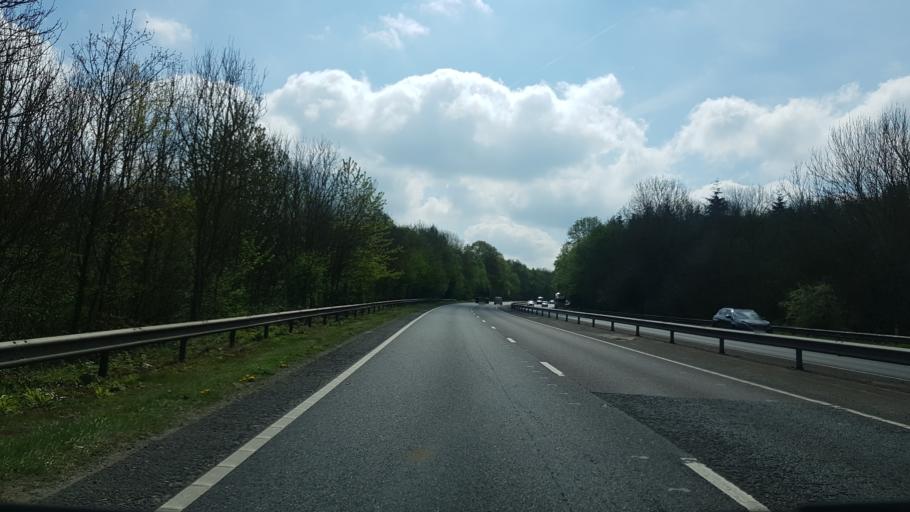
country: GB
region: England
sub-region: Kent
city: Sevenoaks
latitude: 51.2679
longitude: 0.1674
